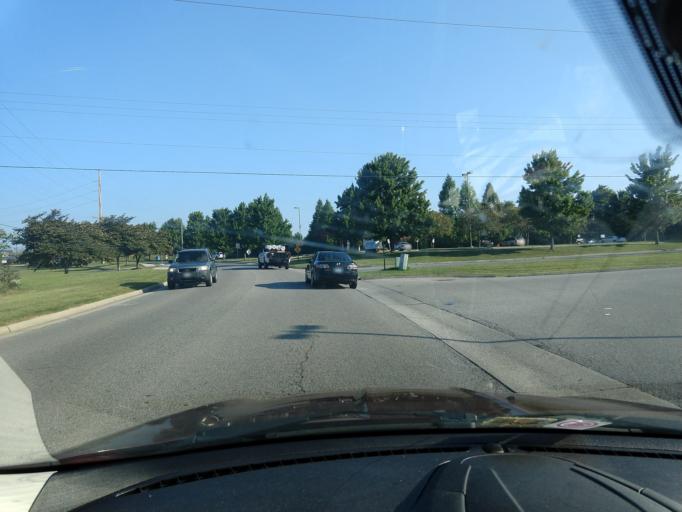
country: US
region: Virginia
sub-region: Montgomery County
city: Merrimac
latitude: 37.1673
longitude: -80.4174
